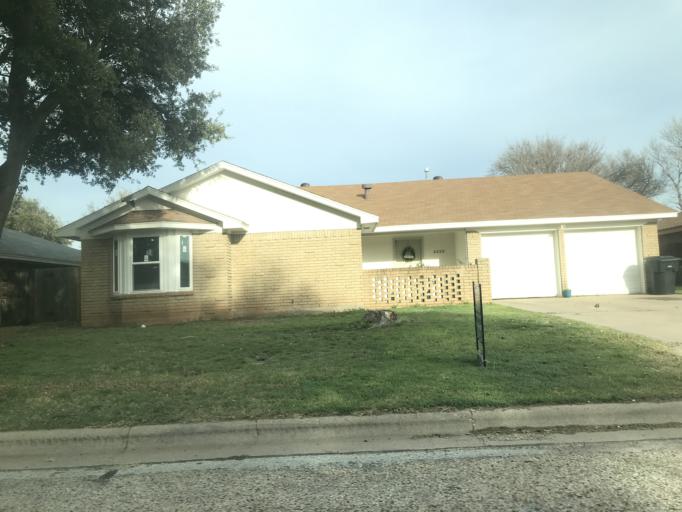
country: US
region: Texas
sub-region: Taylor County
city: Abilene
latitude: 32.3958
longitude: -99.7705
